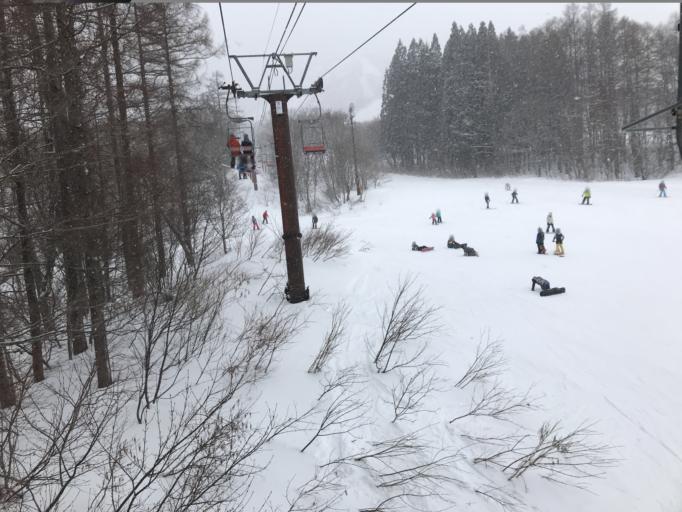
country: JP
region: Nagano
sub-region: Kitaazumi Gun
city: Hakuba
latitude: 36.7532
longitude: 137.8650
